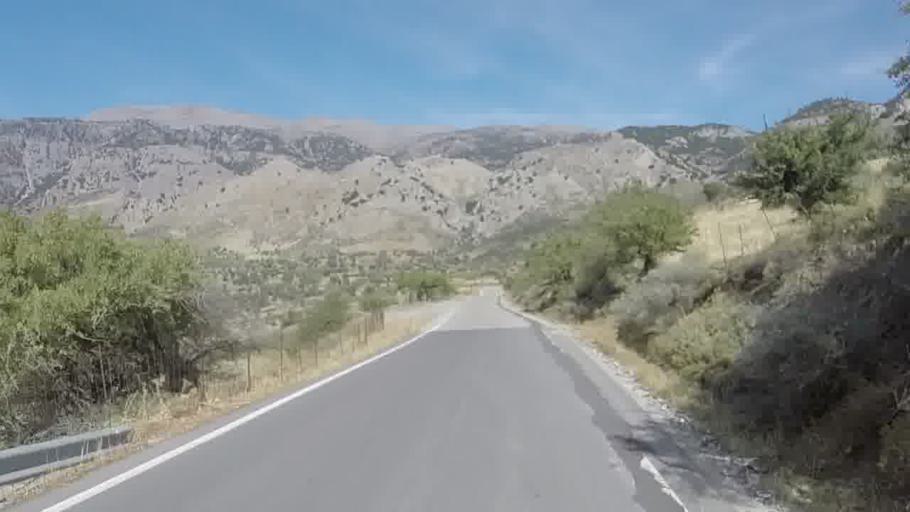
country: GR
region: Crete
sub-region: Nomos Rethymnis
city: Agia Galini
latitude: 35.1796
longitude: 24.7383
